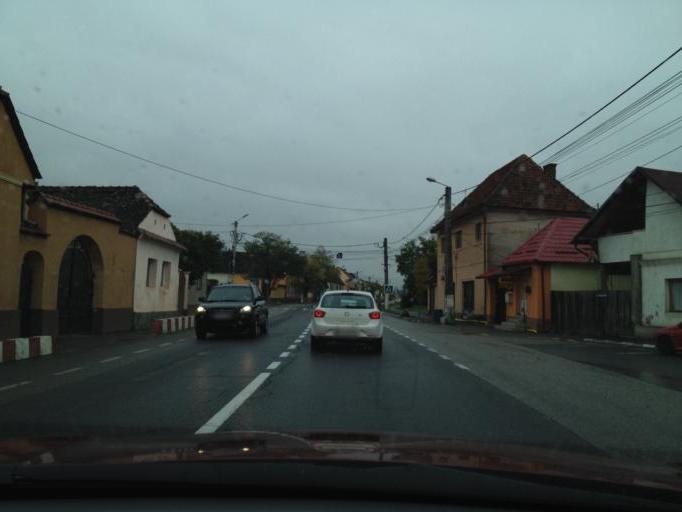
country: RO
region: Brasov
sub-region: Comuna Cristian
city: Cristian
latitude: 45.6286
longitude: 25.4850
